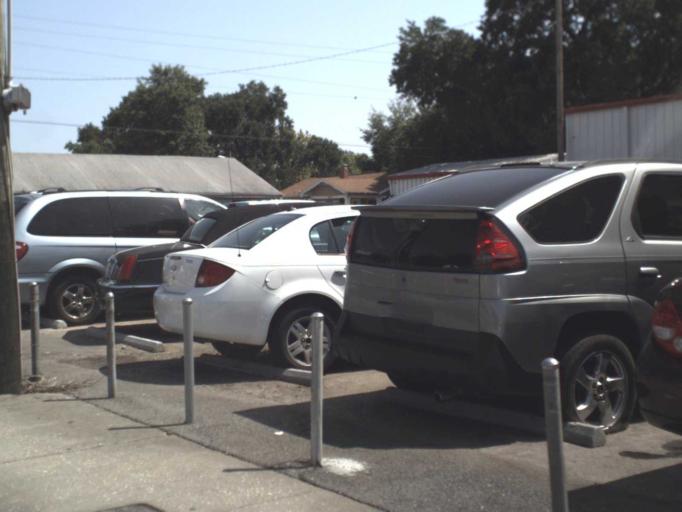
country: US
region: Florida
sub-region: Hillsborough County
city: Egypt Lake-Leto
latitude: 28.0038
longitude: -82.4594
